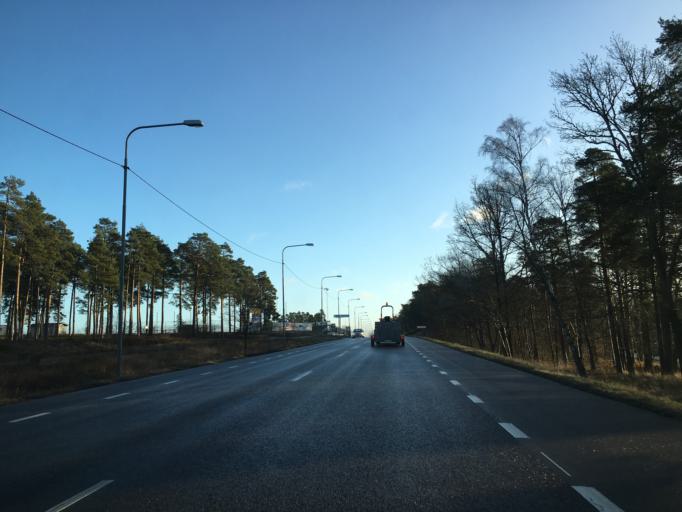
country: SE
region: Kalmar
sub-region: Vasterviks Kommun
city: Vaestervik
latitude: 57.7681
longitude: 16.5835
